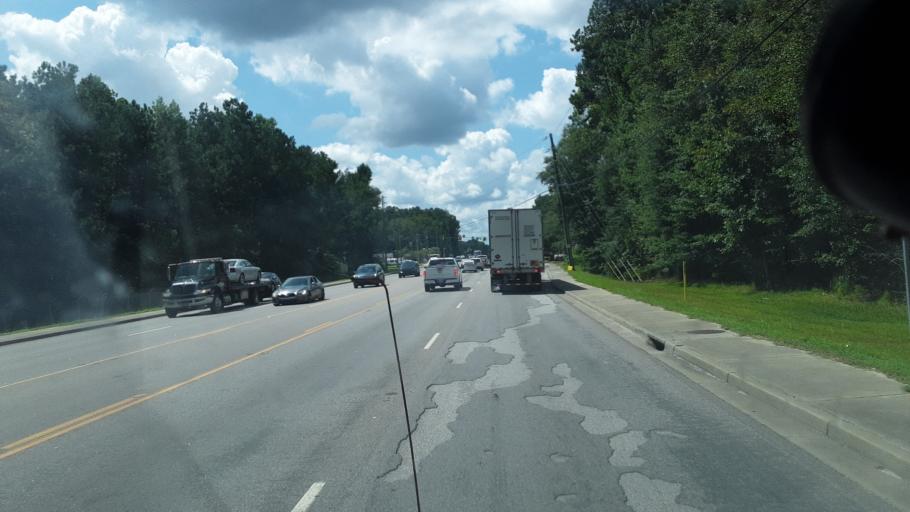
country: US
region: South Carolina
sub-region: Berkeley County
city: Sangaree
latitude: 33.0652
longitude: -80.0922
